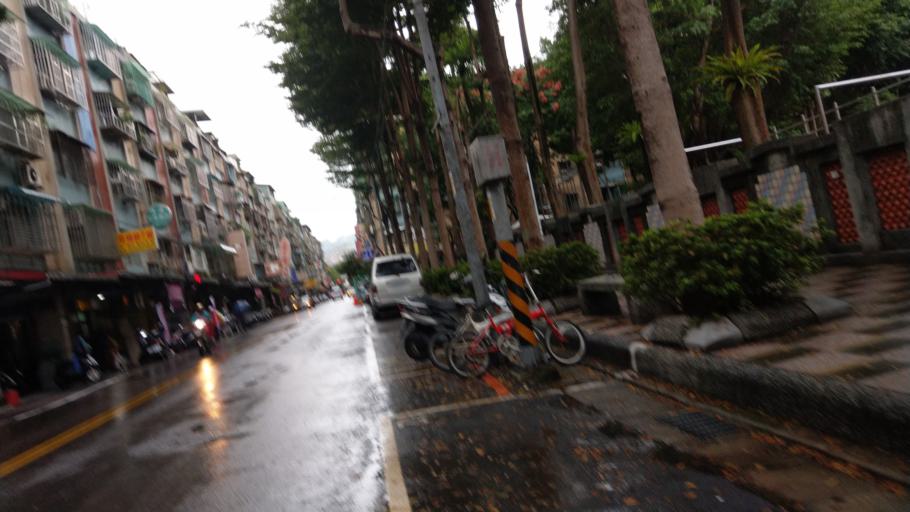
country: TW
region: Taipei
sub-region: Taipei
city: Banqiao
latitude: 24.9948
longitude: 121.4637
